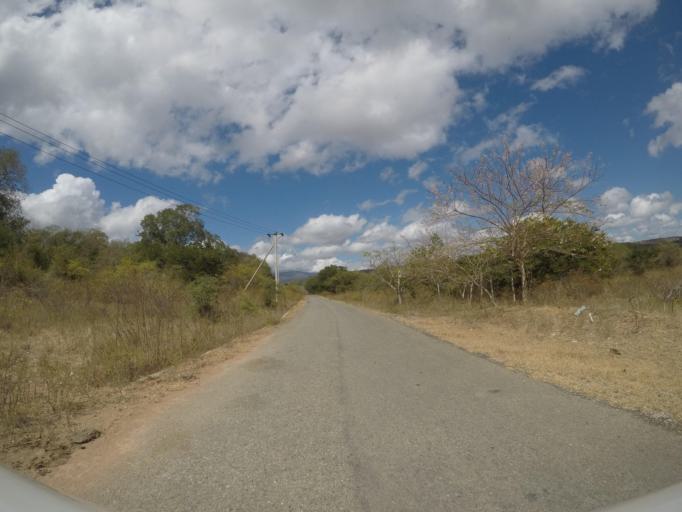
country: TL
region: Lautem
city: Lospalos
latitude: -8.4371
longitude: 126.8280
